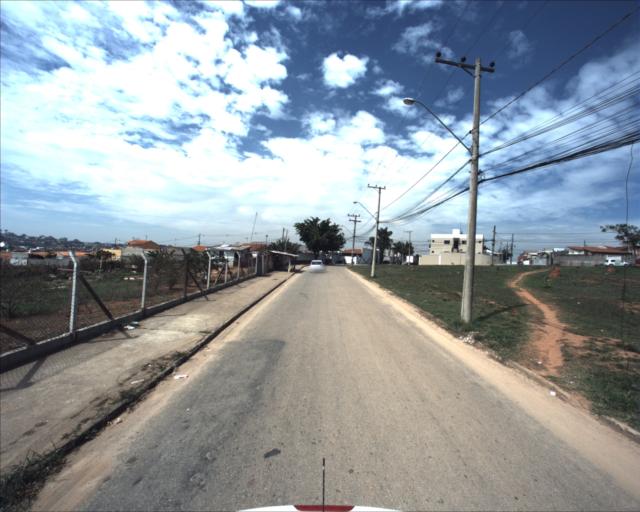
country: BR
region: Sao Paulo
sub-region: Sorocaba
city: Sorocaba
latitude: -23.4862
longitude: -47.5008
